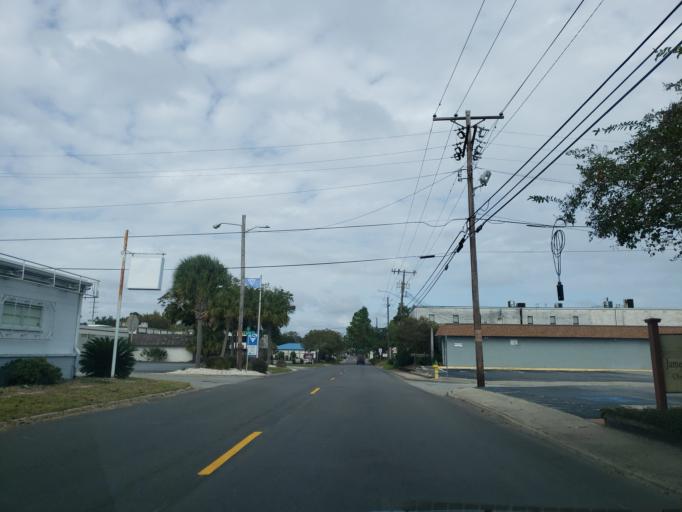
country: US
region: Georgia
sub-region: Chatham County
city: Thunderbolt
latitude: 32.0279
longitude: -81.0969
